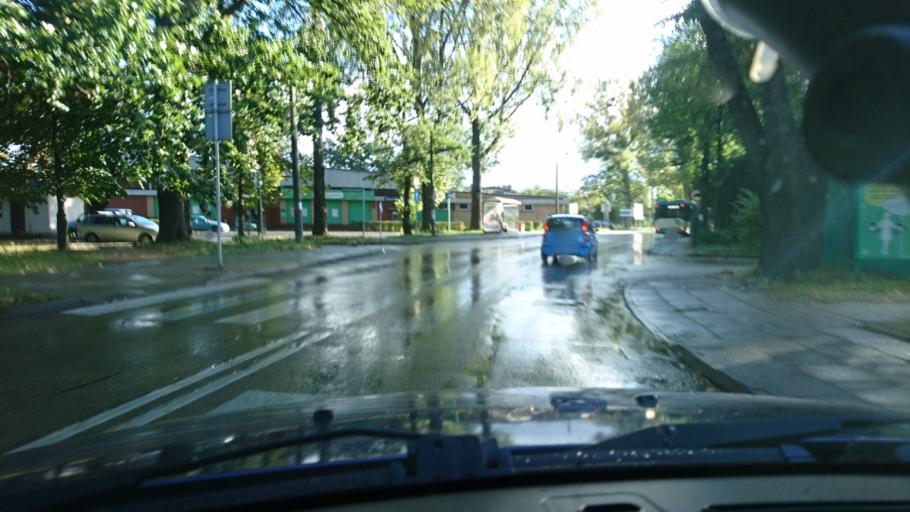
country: PL
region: Silesian Voivodeship
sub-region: Bielsko-Biala
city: Bielsko-Biala
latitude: 49.8548
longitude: 19.0406
